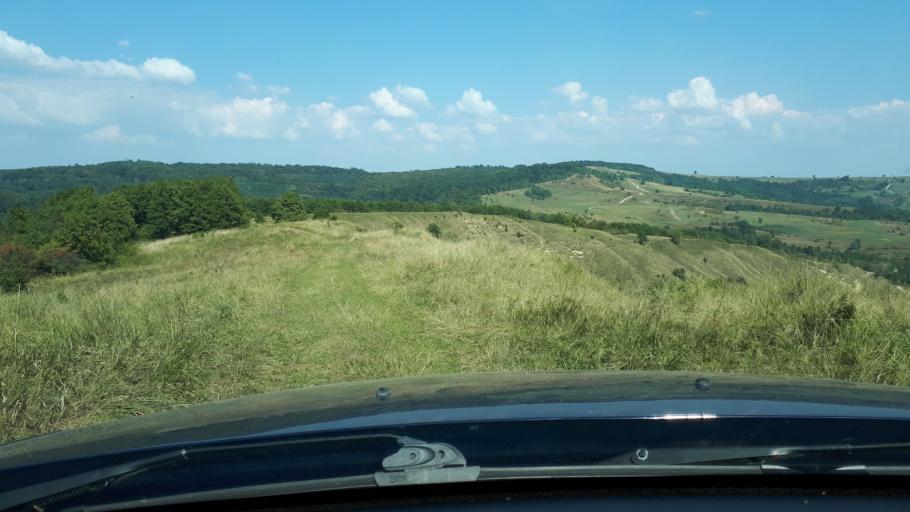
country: RO
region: Brasov
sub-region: Comuna Vistea de Jos
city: Vistea de Jos
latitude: 45.8214
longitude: 24.7484
